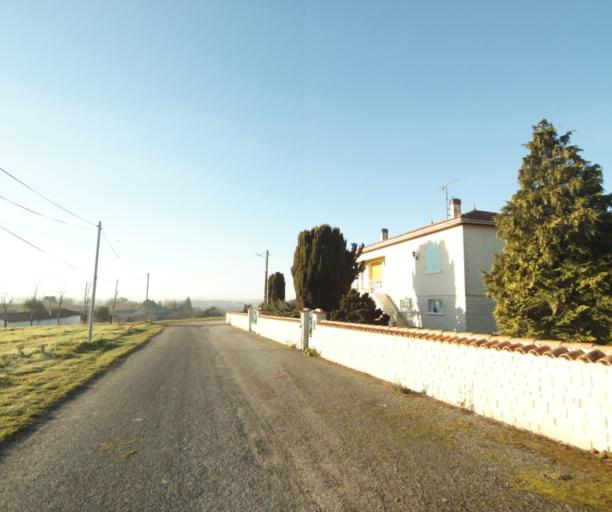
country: FR
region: Poitou-Charentes
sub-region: Departement de la Charente-Maritime
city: Cherac
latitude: 45.6900
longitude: -0.4240
